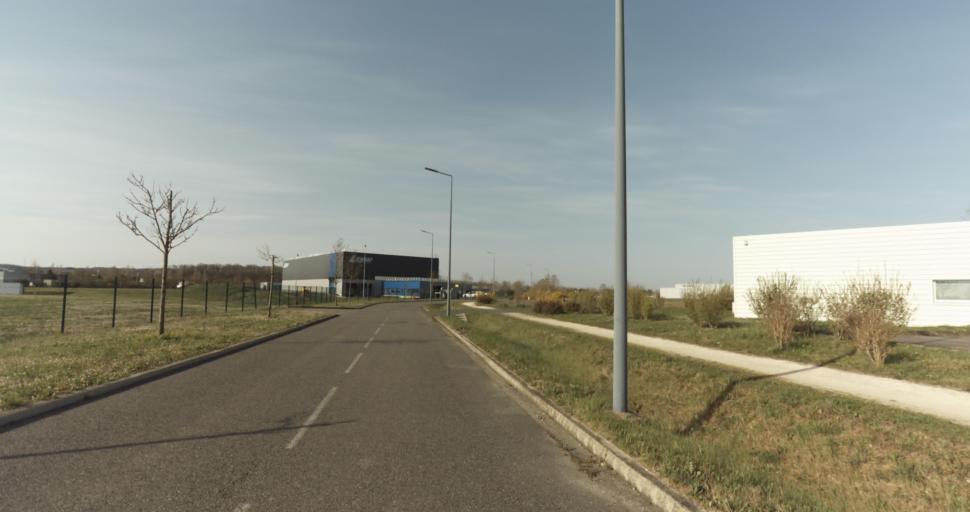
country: FR
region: Midi-Pyrenees
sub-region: Departement du Tarn
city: Saint-Sulpice-la-Pointe
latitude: 43.7656
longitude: 1.7137
